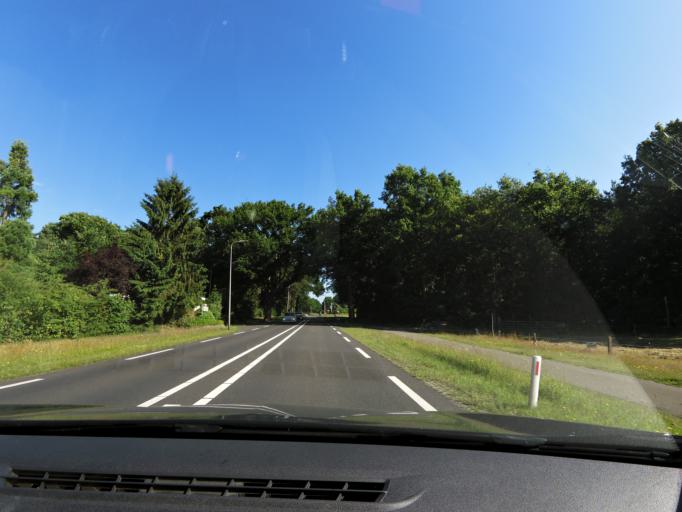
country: NL
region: Overijssel
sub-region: Gemeente Twenterand
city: Den Ham
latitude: 52.4948
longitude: 6.4228
